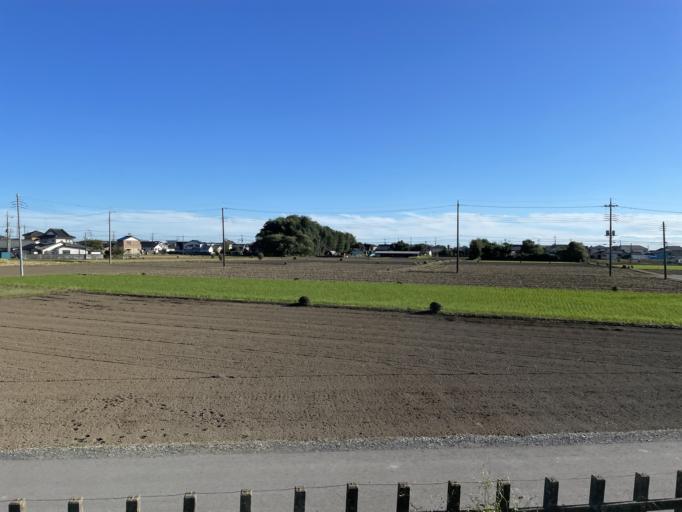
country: JP
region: Tochigi
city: Mibu
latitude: 36.4079
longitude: 139.7706
